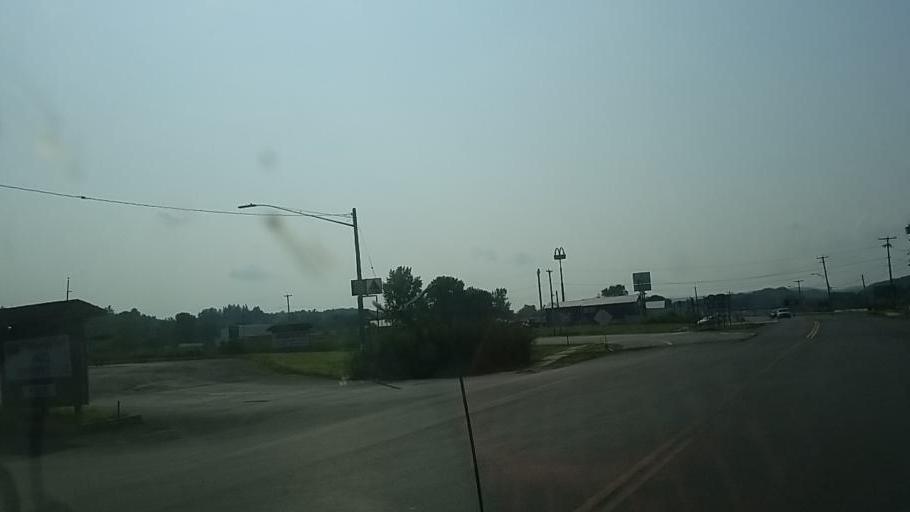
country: US
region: New York
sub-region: Montgomery County
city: Fonda
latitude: 42.9484
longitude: -74.3572
